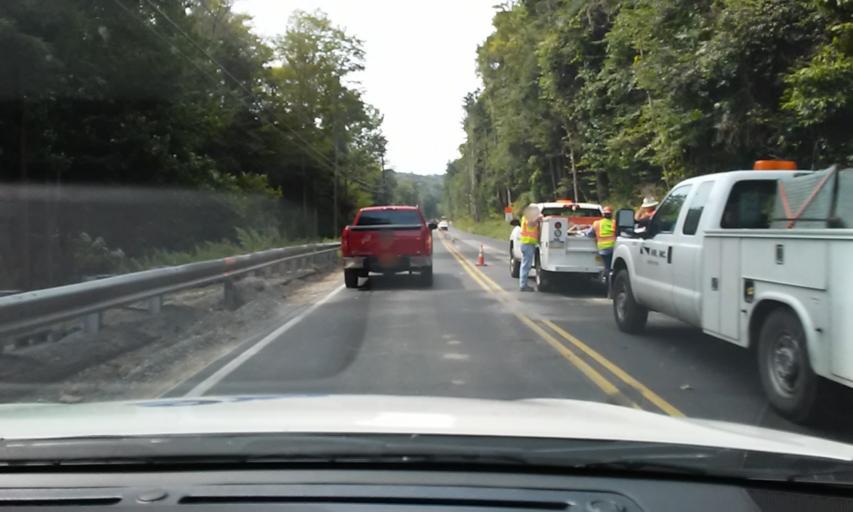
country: US
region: Pennsylvania
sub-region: Clearfield County
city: Treasure Lake
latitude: 41.1839
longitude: -78.6081
